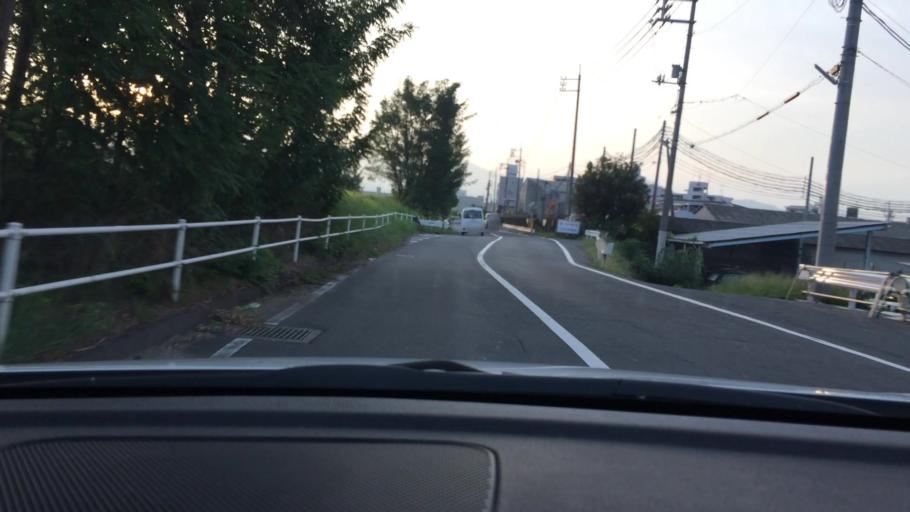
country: JP
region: Hiroshima
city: Hiroshima-shi
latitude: 34.3868
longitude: 132.4865
